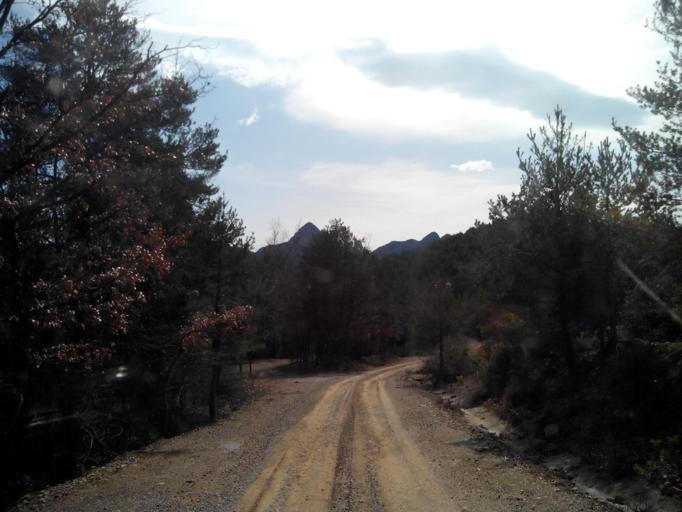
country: ES
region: Catalonia
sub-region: Provincia de Barcelona
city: Vilada
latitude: 42.1456
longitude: 1.9301
